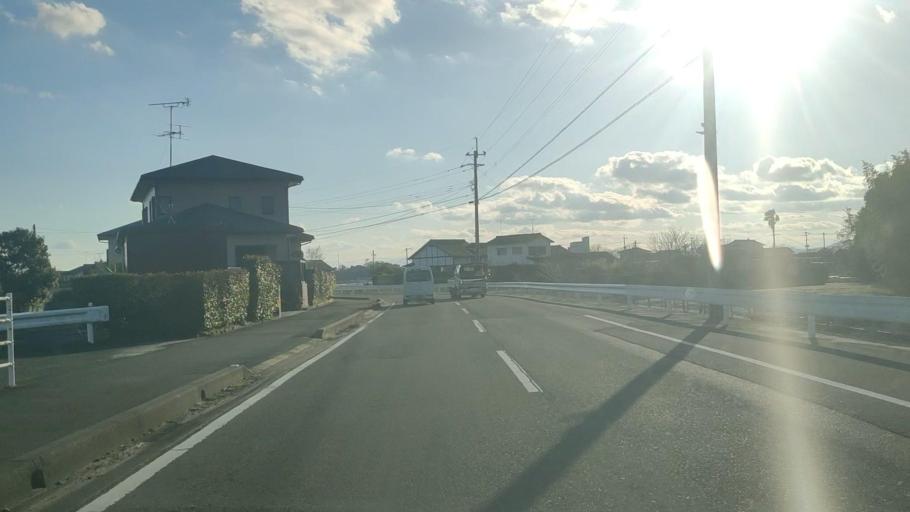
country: JP
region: Saga Prefecture
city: Saga-shi
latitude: 33.3070
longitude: 130.2587
